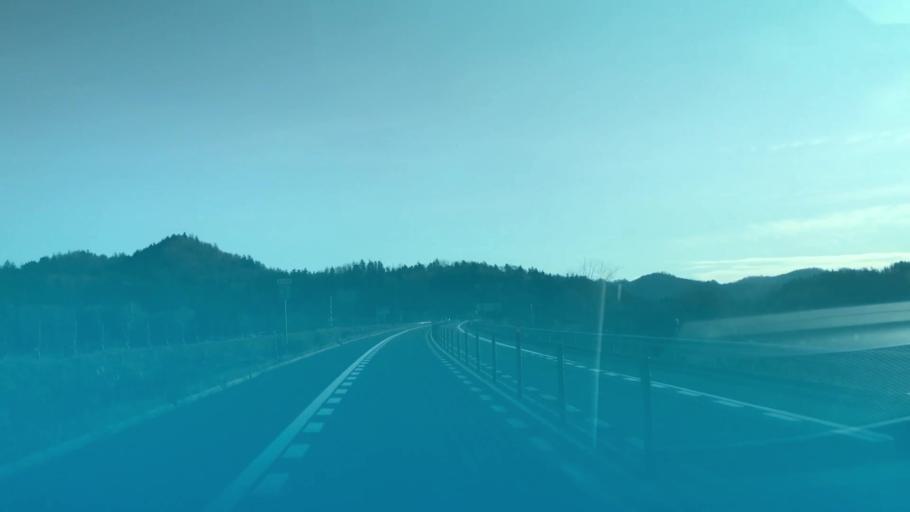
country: JP
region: Hokkaido
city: Iwamizawa
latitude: 42.9328
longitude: 142.0525
